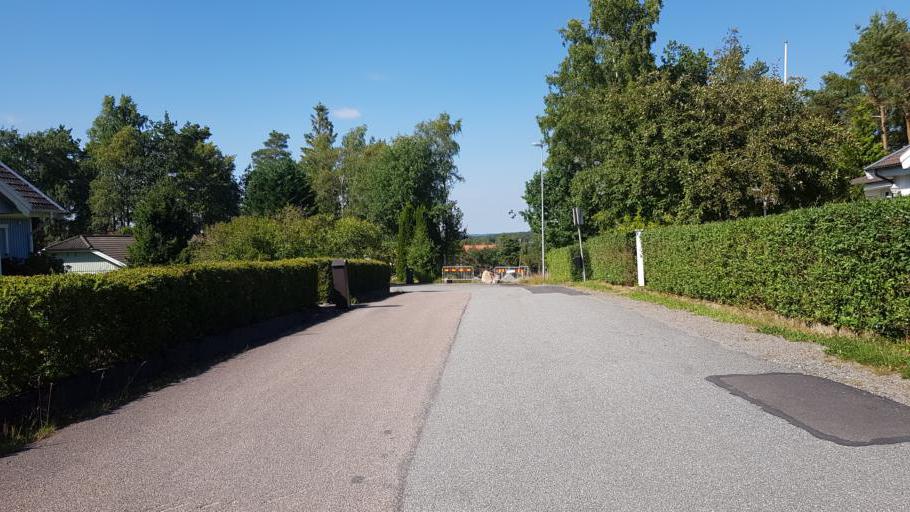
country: SE
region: Vaestra Goetaland
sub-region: Partille Kommun
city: Furulund
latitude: 57.6970
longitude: 12.1447
